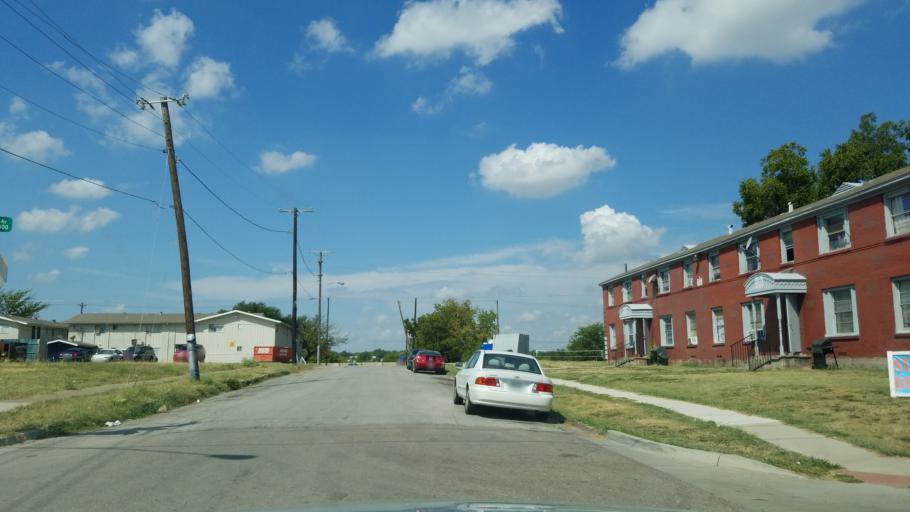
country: US
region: Texas
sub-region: Dallas County
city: Dallas
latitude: 32.7528
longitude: -96.8135
